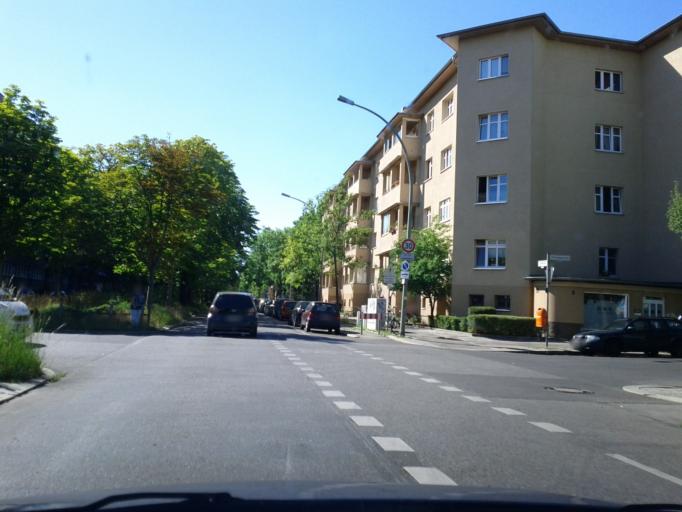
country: DE
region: Berlin
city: Prenzlauer Berg Bezirk
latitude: 52.5428
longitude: 13.4350
